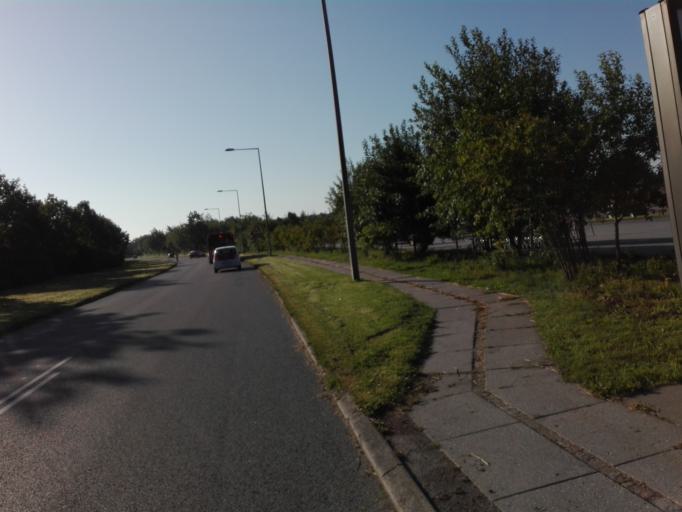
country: DK
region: Central Jutland
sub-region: Arhus Kommune
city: Tranbjerg
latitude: 56.0916
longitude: 10.1369
